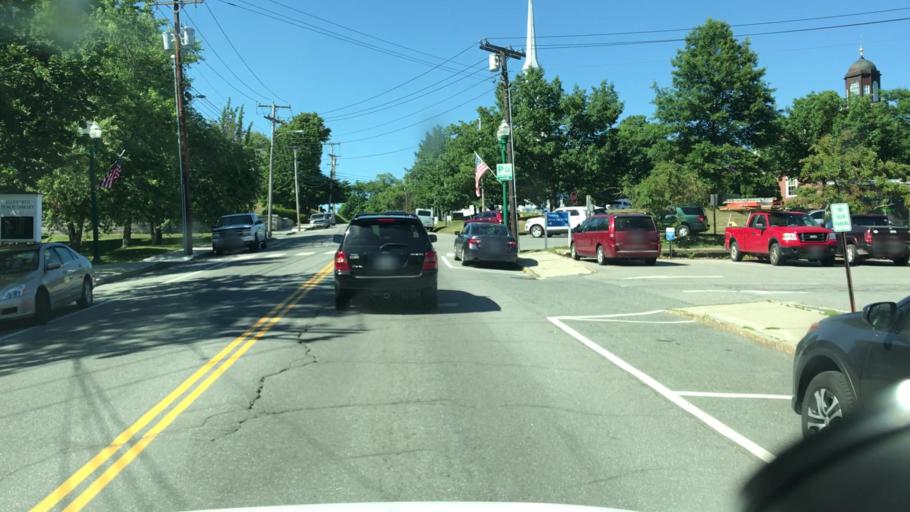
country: US
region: Maine
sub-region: Hancock County
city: Ellsworth
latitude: 44.5417
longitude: -68.4251
